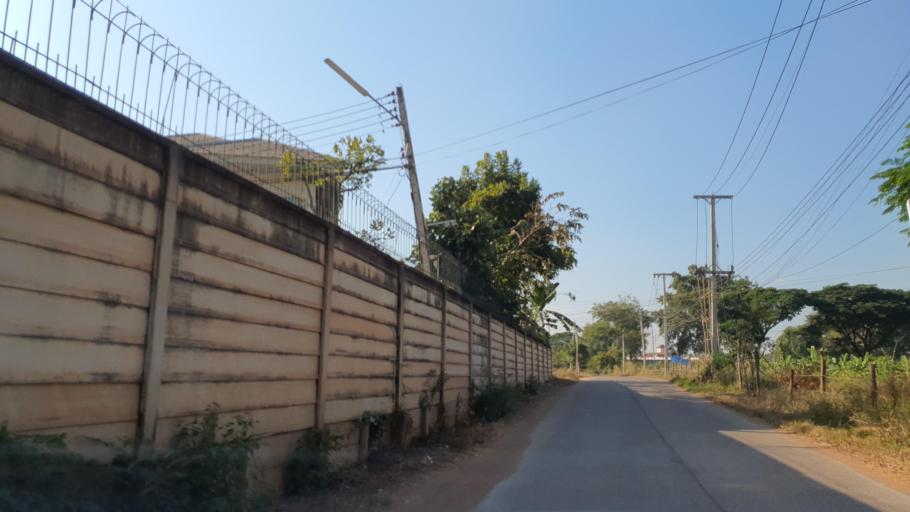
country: TH
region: Khon Kaen
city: Khon Kaen
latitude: 16.4141
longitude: 102.8120
